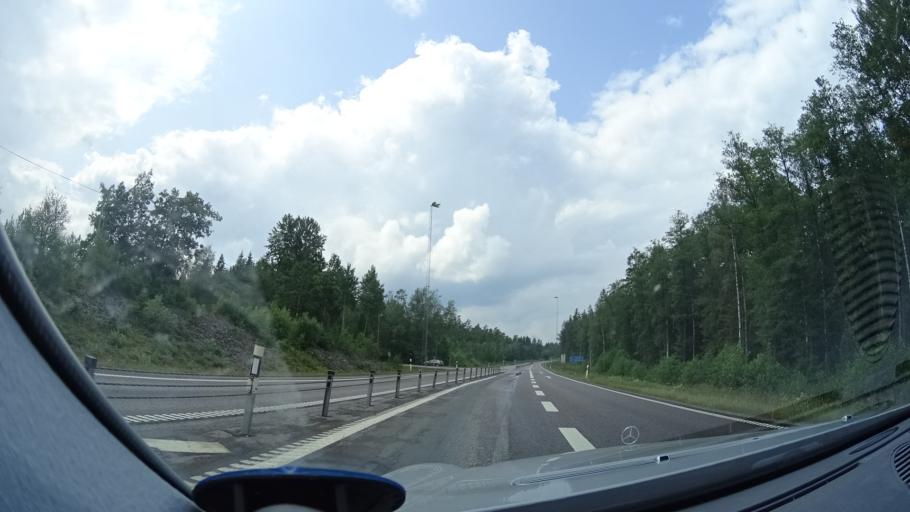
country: SE
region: Kalmar
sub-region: Nybro Kommun
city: Nybro
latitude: 56.7075
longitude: 15.7320
